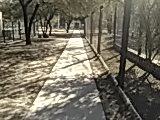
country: AR
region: Chaco
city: Presidencia Roque Saenz Pena
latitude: -26.8192
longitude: -60.4171
